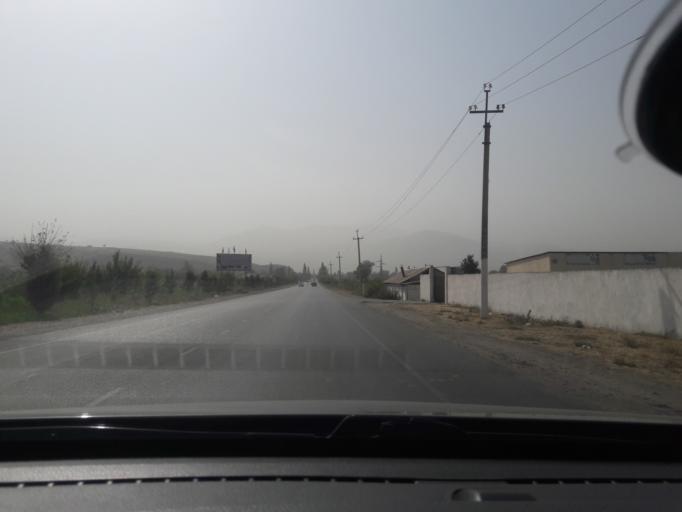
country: TJ
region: Republican Subordination
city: Vahdat
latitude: 38.5299
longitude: 69.0260
